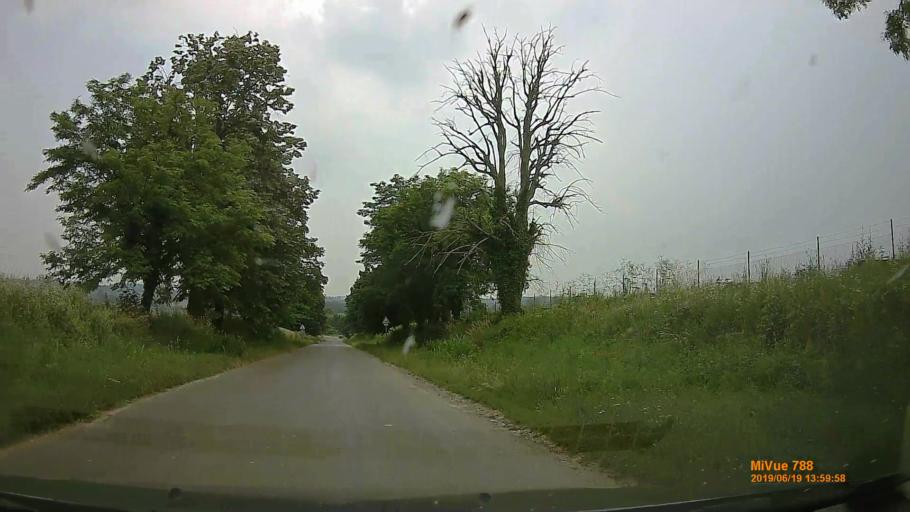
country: HU
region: Baranya
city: Szigetvar
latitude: 46.0866
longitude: 17.8000
